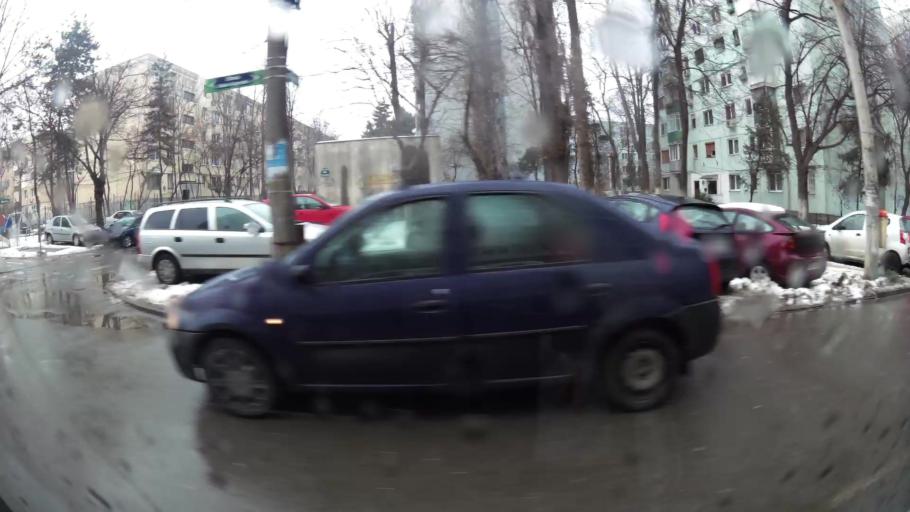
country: RO
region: Ilfov
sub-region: Comuna Chiajna
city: Rosu
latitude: 44.4159
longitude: 26.0171
